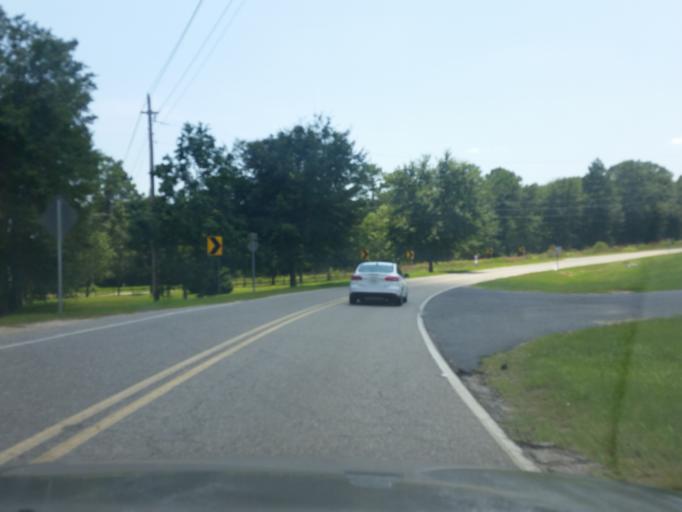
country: US
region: Alabama
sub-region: Baldwin County
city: Robertsdale
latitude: 30.6271
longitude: -87.6155
